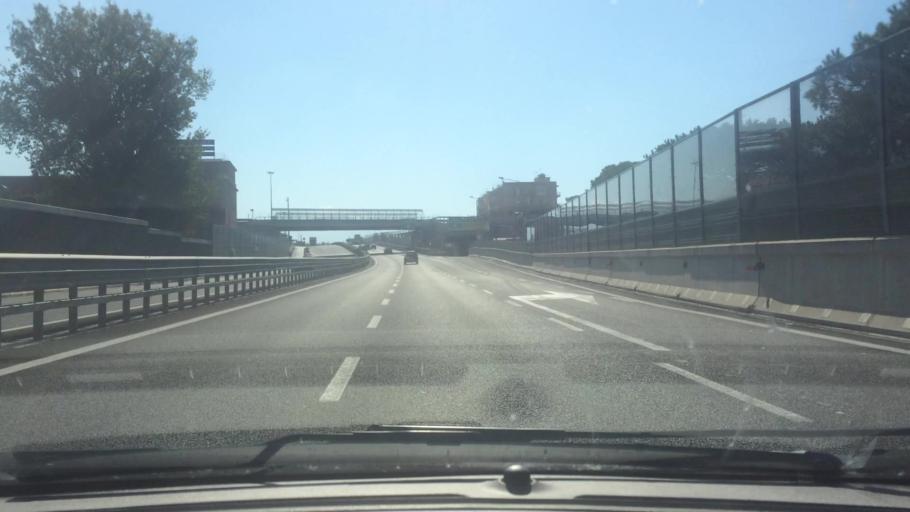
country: IT
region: Campania
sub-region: Provincia di Napoli
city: Ercolano
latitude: 40.8183
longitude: 14.3536
